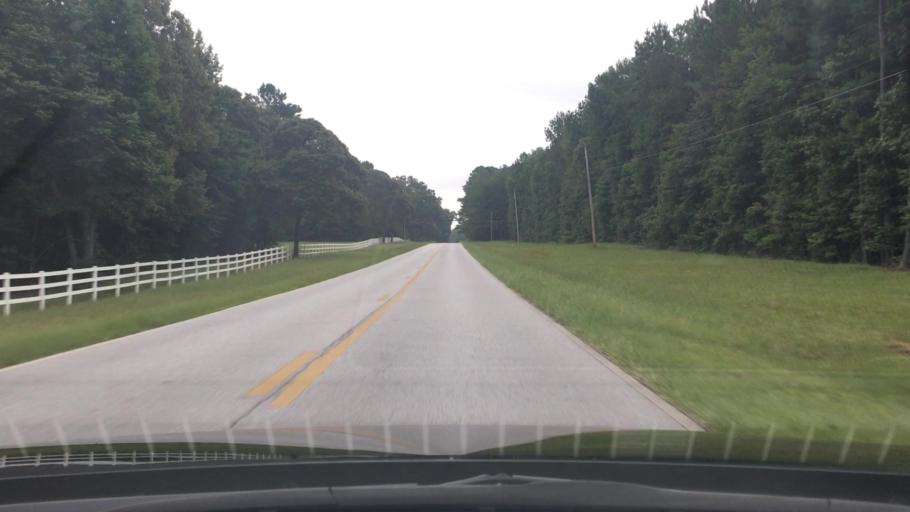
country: US
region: Georgia
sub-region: Spalding County
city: Experiment
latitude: 33.2807
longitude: -84.4082
